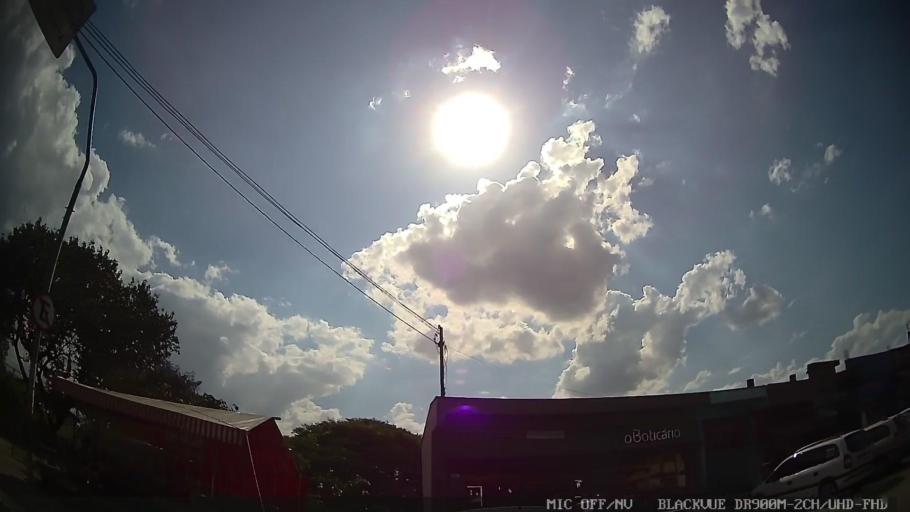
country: BR
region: Sao Paulo
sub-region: Ferraz De Vasconcelos
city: Ferraz de Vasconcelos
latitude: -23.5227
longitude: -46.4184
